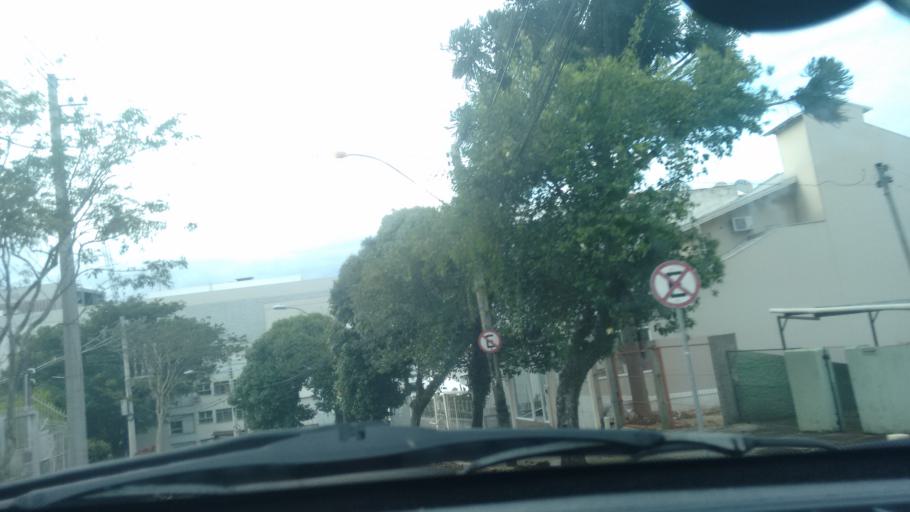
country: BR
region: Rio Grande do Sul
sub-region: Porto Alegre
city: Porto Alegre
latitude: -30.0095
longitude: -51.1617
